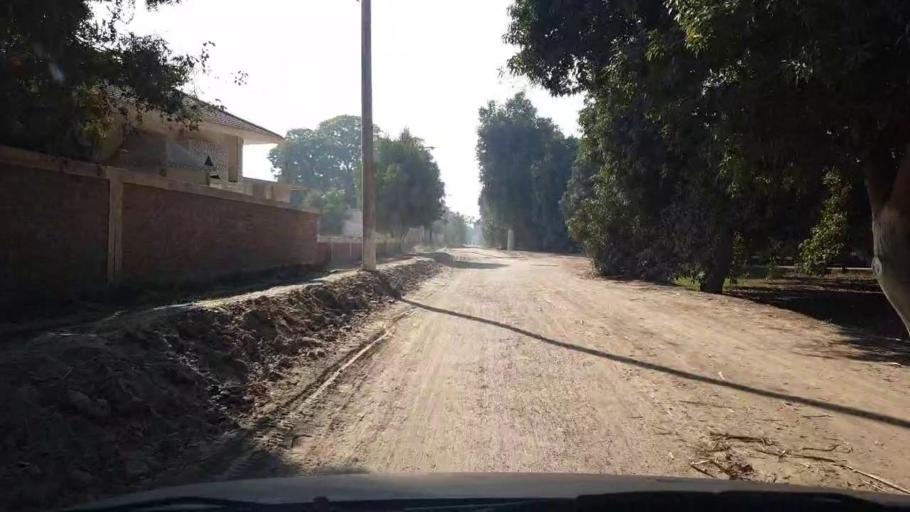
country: PK
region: Sindh
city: Tando Jam
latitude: 25.4402
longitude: 68.6017
